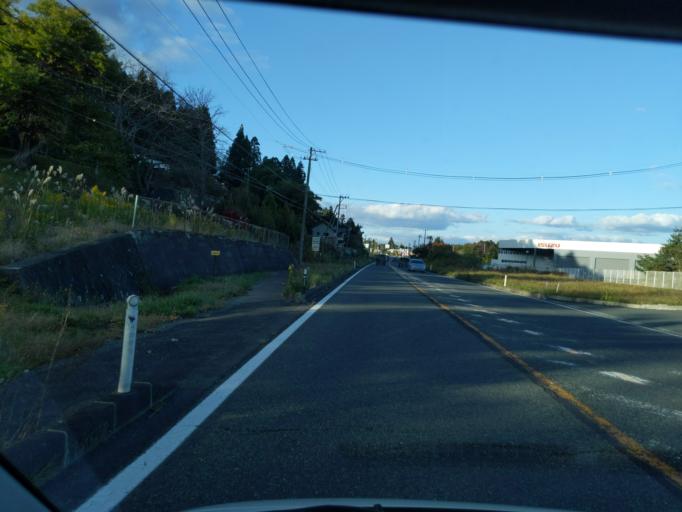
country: JP
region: Iwate
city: Kitakami
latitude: 39.2470
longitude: 141.0993
